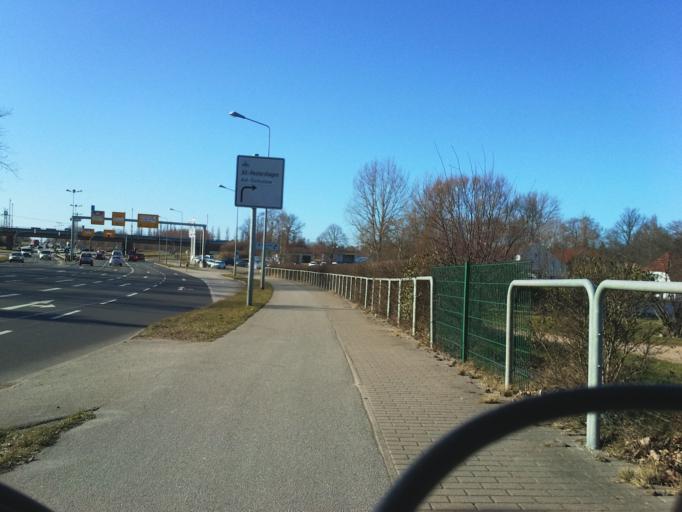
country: DE
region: Mecklenburg-Vorpommern
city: Lambrechtshagen
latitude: 54.1046
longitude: 12.0689
